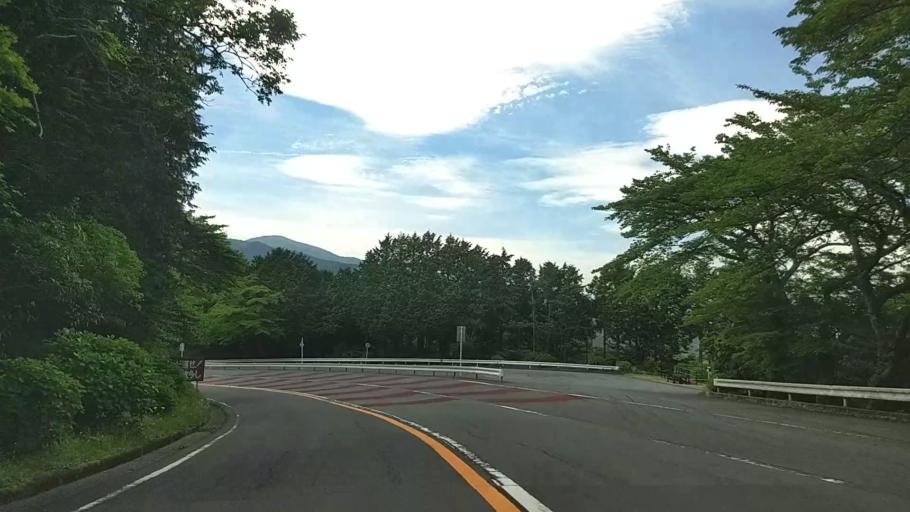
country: JP
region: Kanagawa
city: Odawara
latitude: 35.2191
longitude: 139.1162
